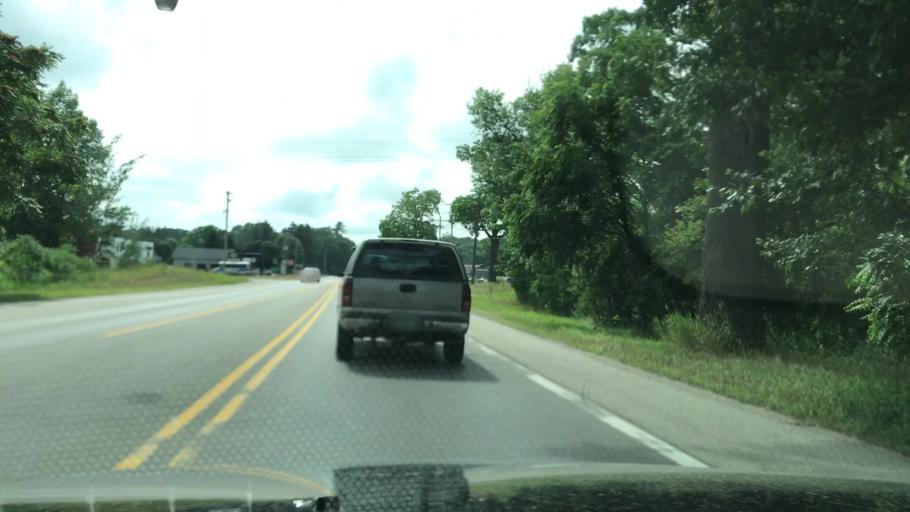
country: US
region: Michigan
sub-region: Ottawa County
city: Spring Lake
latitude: 43.0740
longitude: -86.1569
